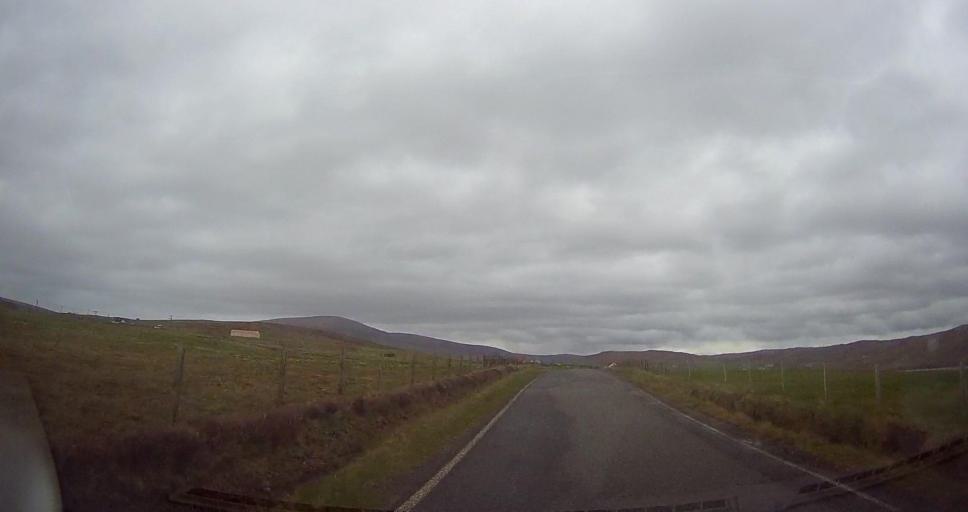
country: GB
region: Scotland
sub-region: Shetland Islands
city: Lerwick
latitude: 60.4804
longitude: -1.4783
